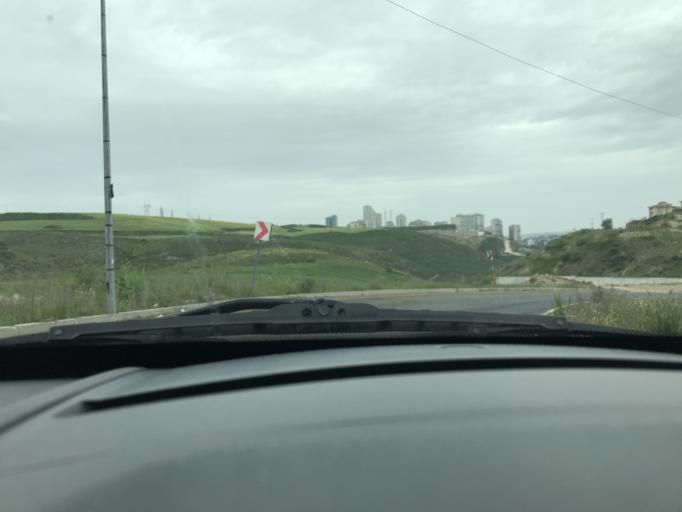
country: TR
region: Istanbul
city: Esenyurt
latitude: 41.0962
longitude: 28.6807
